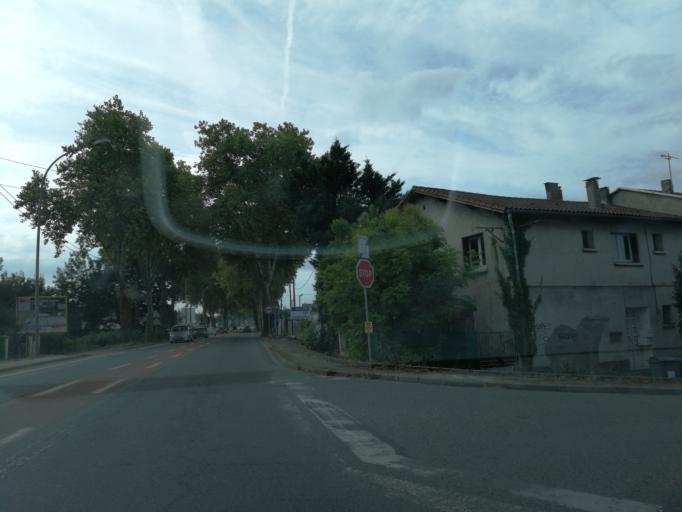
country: FR
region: Midi-Pyrenees
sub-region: Departement de la Haute-Garonne
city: Saint-Alban
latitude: 43.6761
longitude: 1.4087
